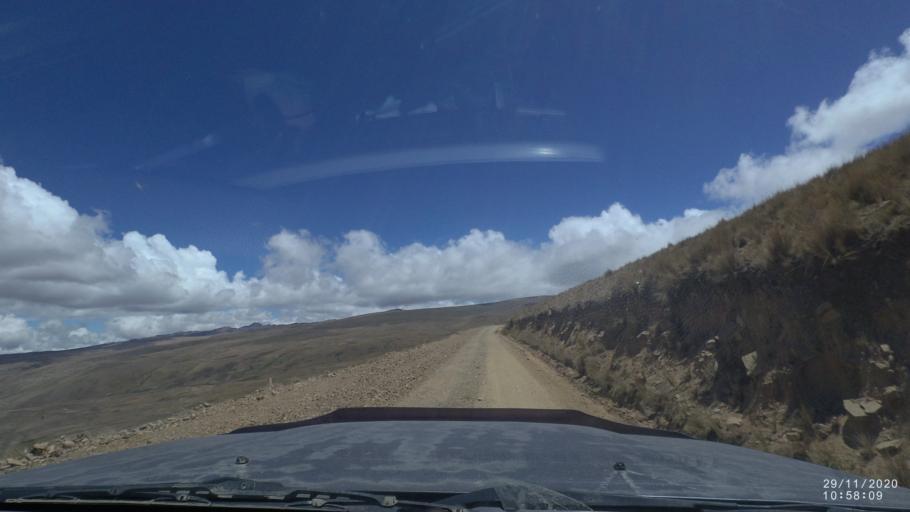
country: BO
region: Cochabamba
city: Cochabamba
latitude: -17.2111
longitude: -66.2314
